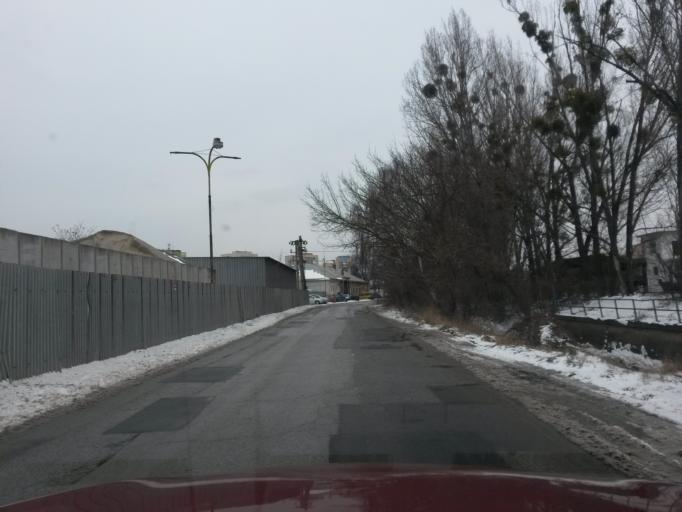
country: SK
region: Kosicky
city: Kosice
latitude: 48.7107
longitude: 21.2701
